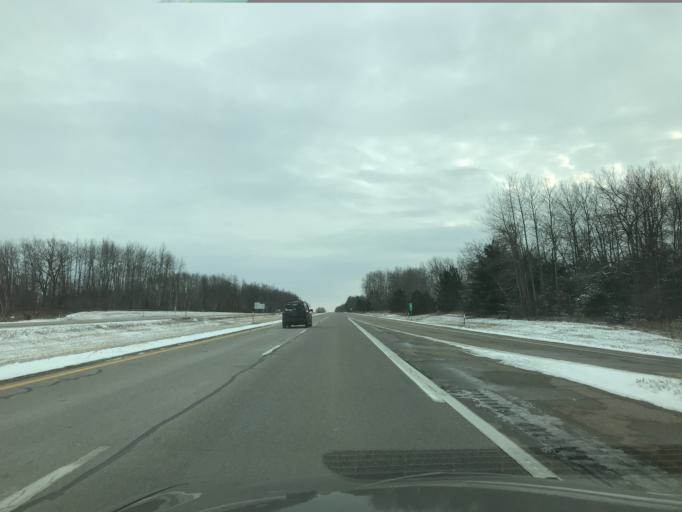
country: US
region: Michigan
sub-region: Roscommon County
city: Houghton Lake
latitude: 44.3331
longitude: -84.8077
